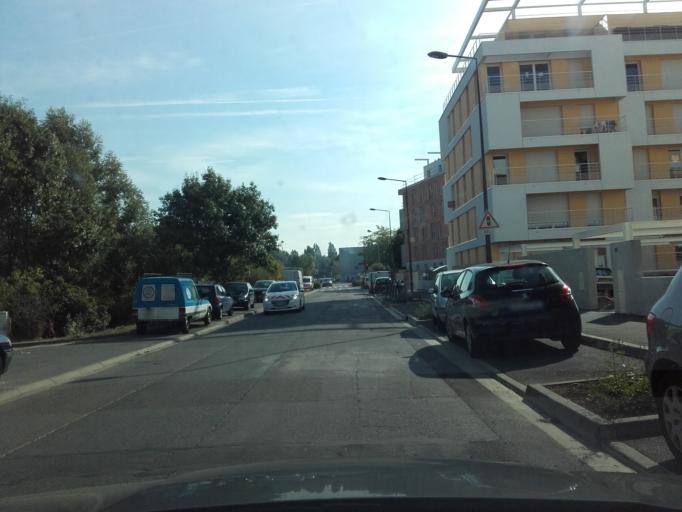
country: FR
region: Centre
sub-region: Departement d'Indre-et-Loire
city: Tours
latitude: 47.3653
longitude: 0.6823
